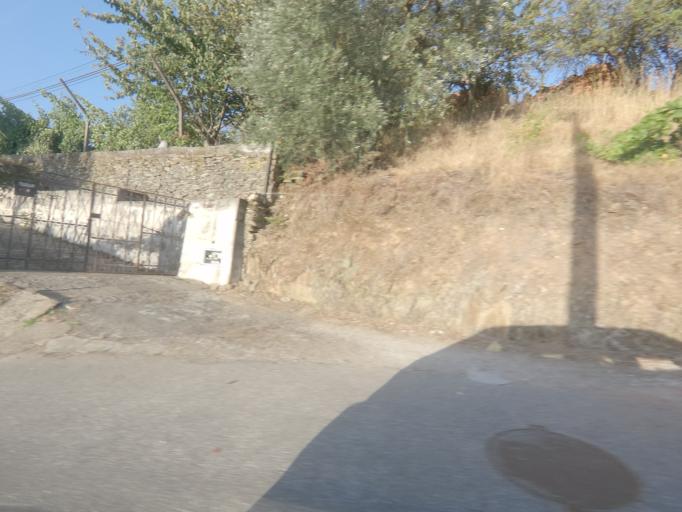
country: PT
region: Viseu
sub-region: Armamar
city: Armamar
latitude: 41.1881
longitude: -7.6887
